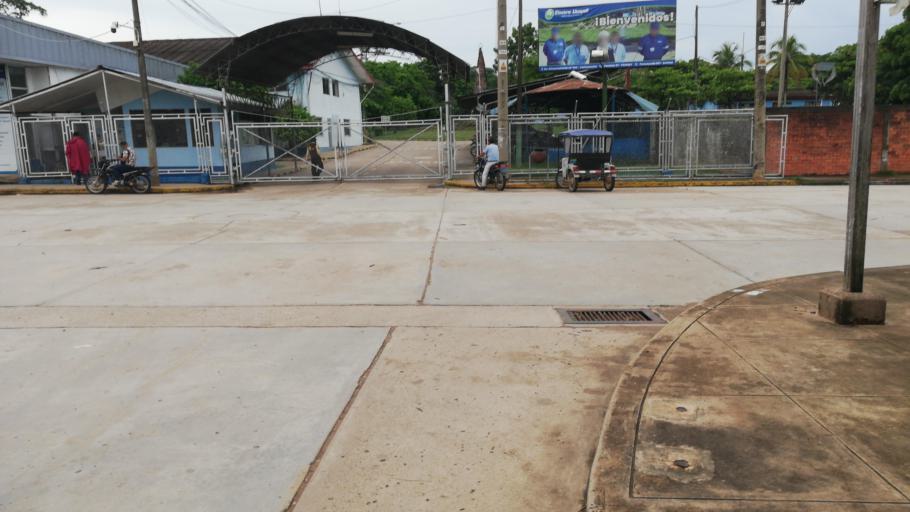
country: PE
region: Ucayali
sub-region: Provincia de Coronel Portillo
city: Puerto Callao
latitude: -8.3520
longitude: -74.5785
